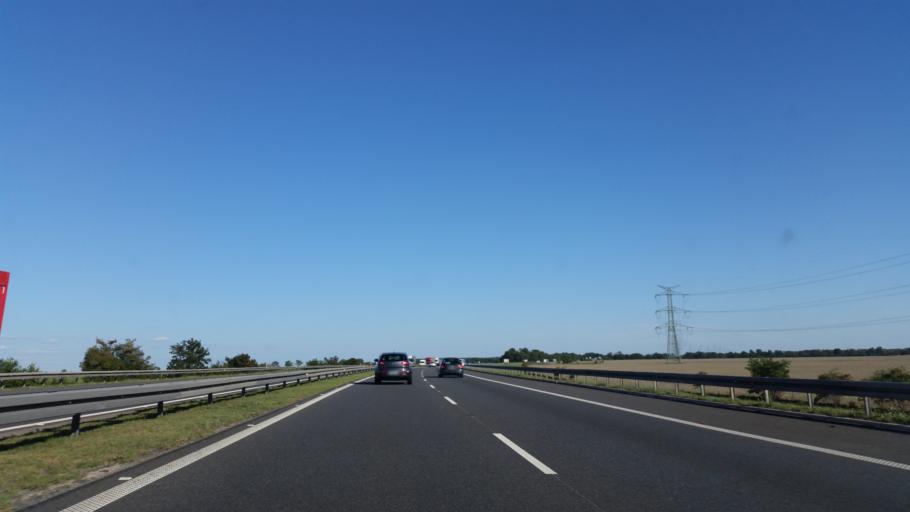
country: PL
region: Lower Silesian Voivodeship
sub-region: Powiat strzelinski
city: Wiazow
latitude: 50.8364
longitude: 17.2794
